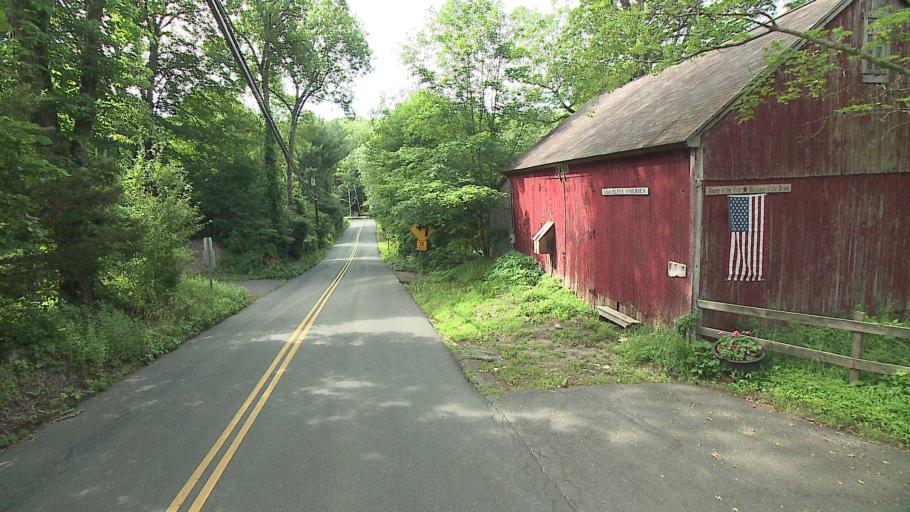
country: US
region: Connecticut
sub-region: New Haven County
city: Southbury
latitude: 41.4294
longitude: -73.2009
